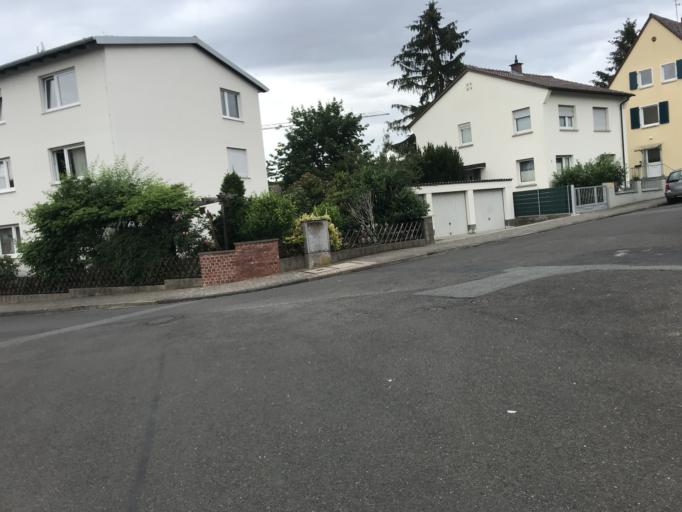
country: DE
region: Rheinland-Pfalz
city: Ingelheim am Rhein
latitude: 49.9732
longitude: 8.0647
